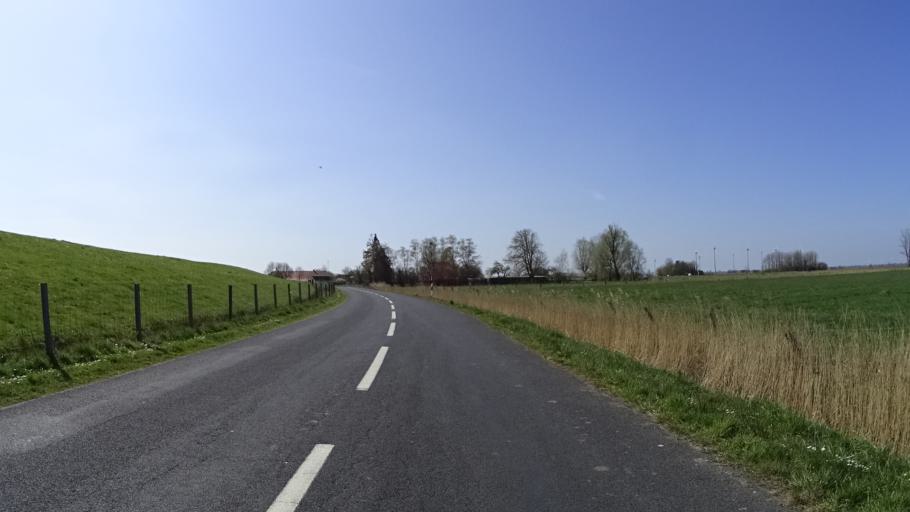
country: DE
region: Lower Saxony
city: Weener
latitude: 53.1964
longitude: 7.4023
